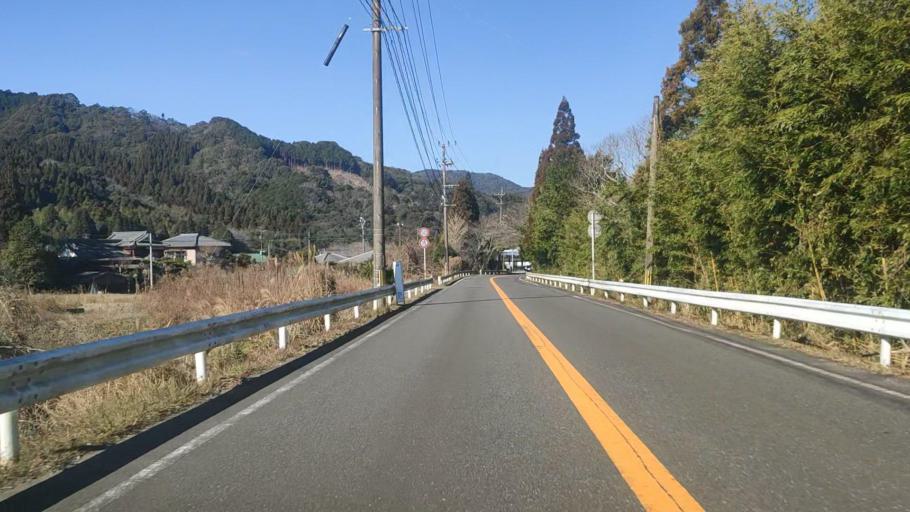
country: JP
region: Oita
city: Saiki
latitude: 32.9006
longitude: 131.9348
